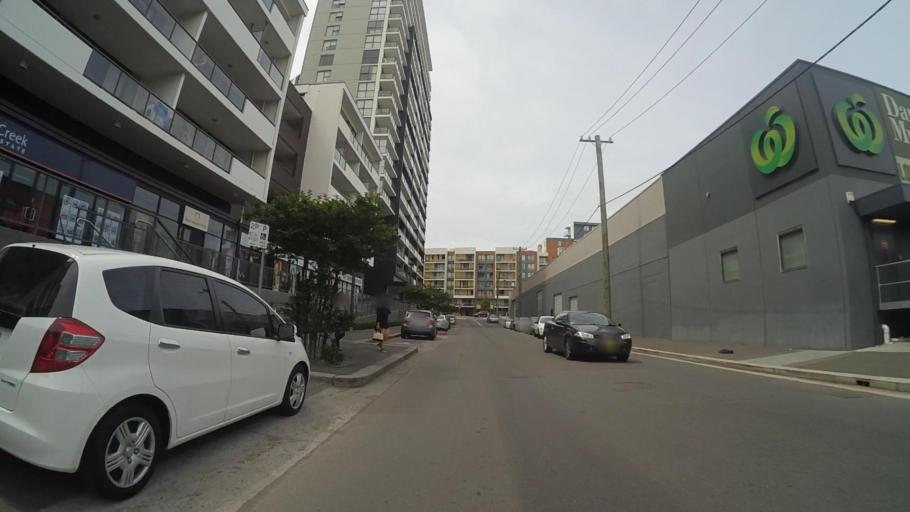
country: AU
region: New South Wales
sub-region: Rockdale
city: Arncliffe
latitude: -33.9308
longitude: 151.1533
